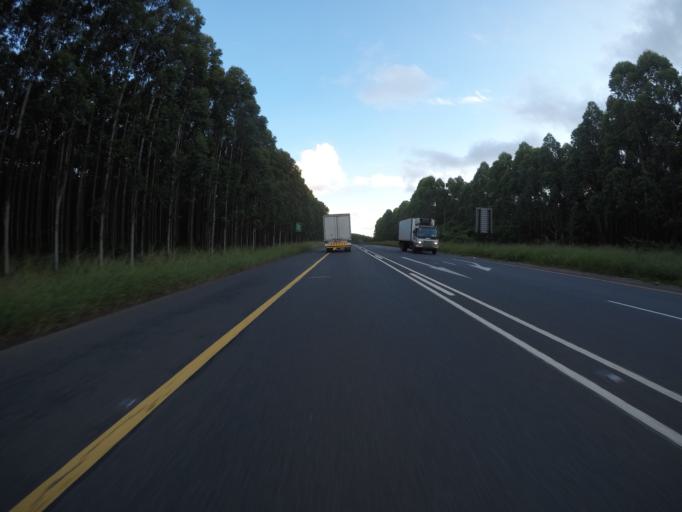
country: ZA
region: KwaZulu-Natal
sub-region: uThungulu District Municipality
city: KwaMbonambi
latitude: -28.5898
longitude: 32.0996
